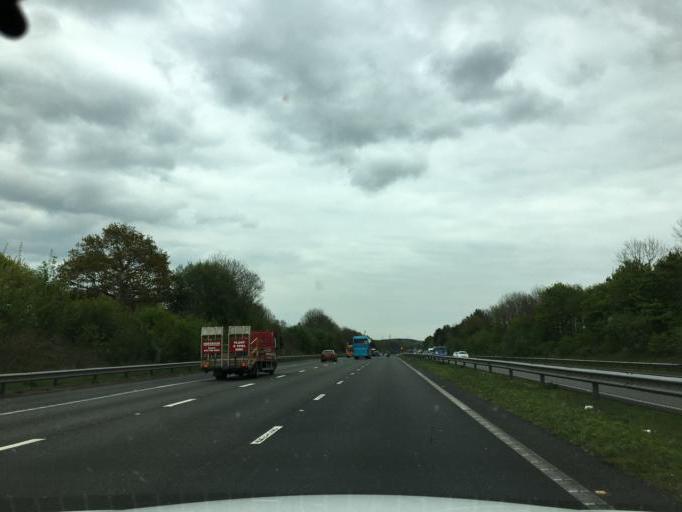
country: GB
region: Wales
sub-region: Caerphilly County Borough
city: Bedwas
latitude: 51.5469
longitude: -3.1748
